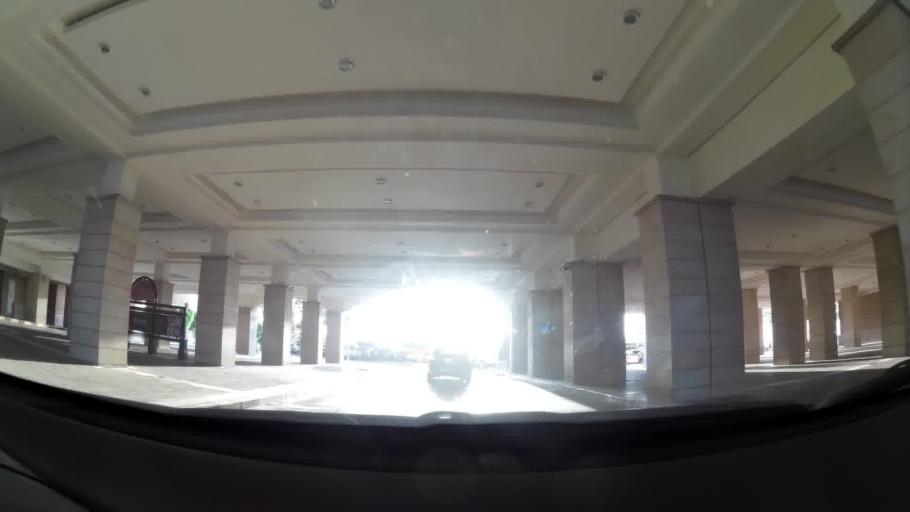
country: KW
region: Al Asimah
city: Kuwait City
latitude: 29.3902
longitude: 47.9811
